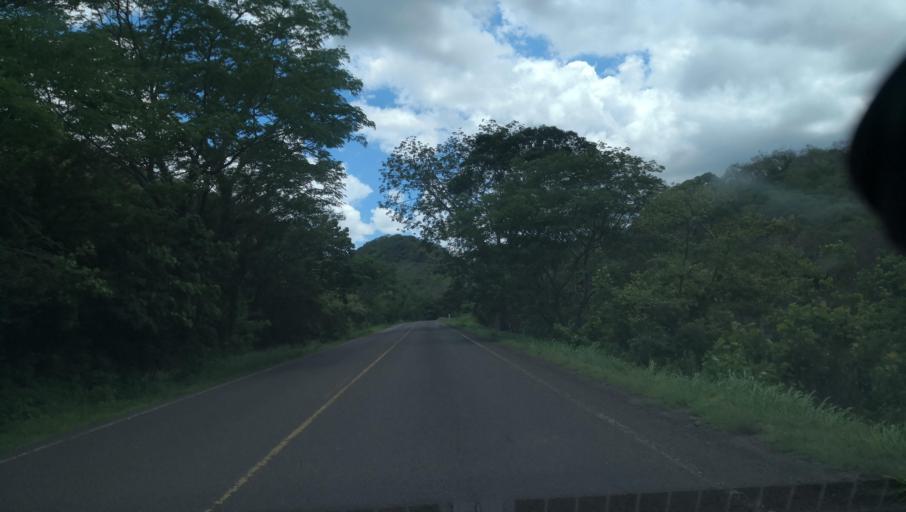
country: NI
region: Madriz
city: Palacaguina
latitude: 13.4360
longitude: -86.4313
